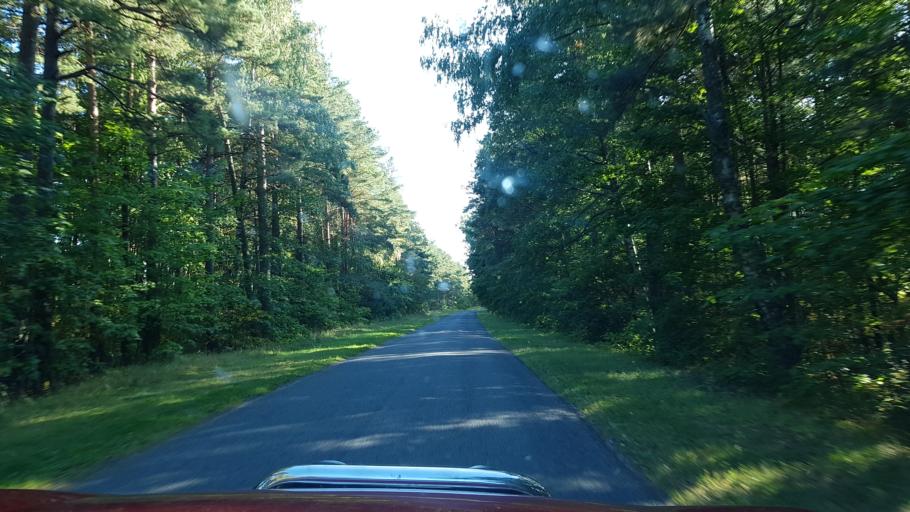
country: LV
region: Salacgrivas
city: Ainazi
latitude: 57.8943
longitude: 24.3720
